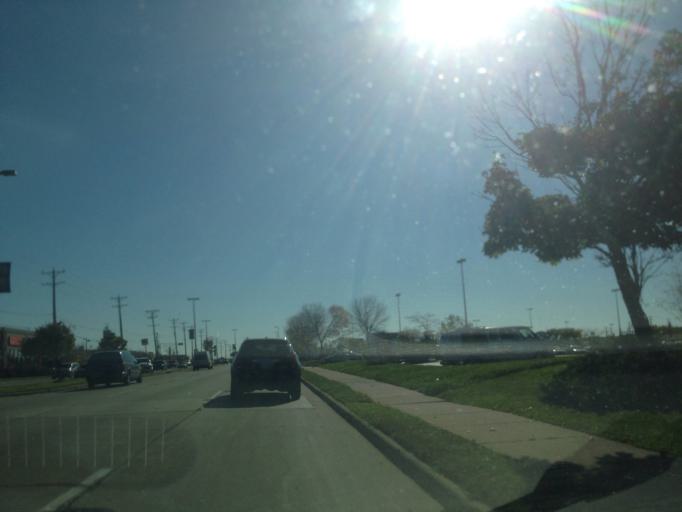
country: US
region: Wisconsin
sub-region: Milwaukee County
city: West Milwaukee
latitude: 43.0162
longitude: -87.9678
